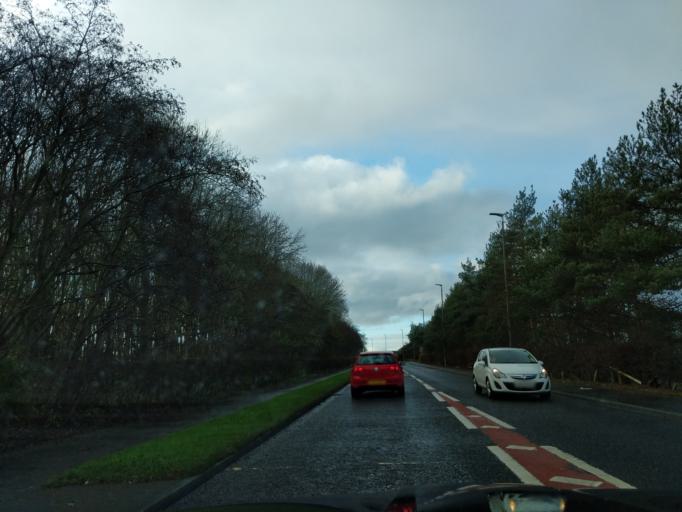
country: GB
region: England
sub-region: Northumberland
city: Blyth
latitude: 55.1051
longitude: -1.5188
